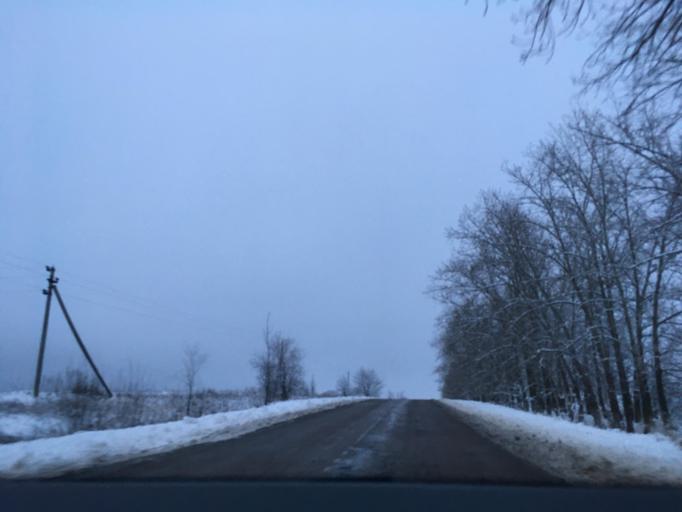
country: RU
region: Voronezj
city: Verkhniy Mamon
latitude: 50.0592
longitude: 40.2597
